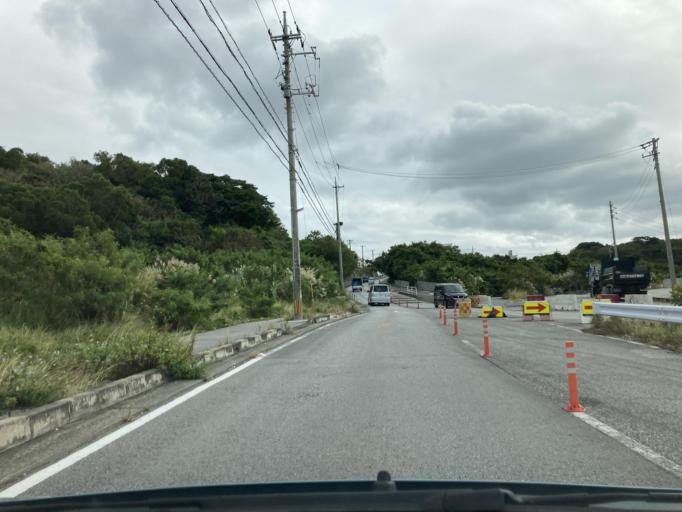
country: JP
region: Okinawa
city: Tomigusuku
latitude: 26.1645
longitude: 127.6790
